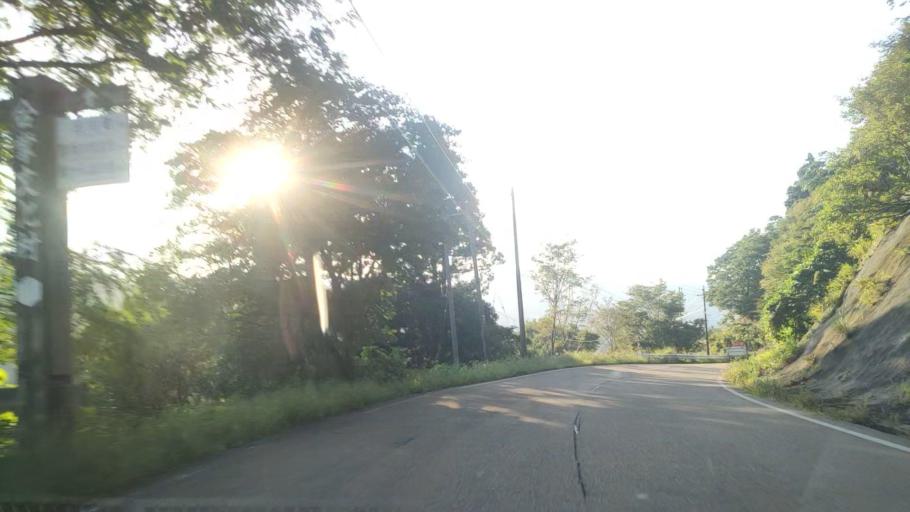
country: JP
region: Toyama
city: Yatsuomachi-higashikumisaka
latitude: 36.5018
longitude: 137.0218
